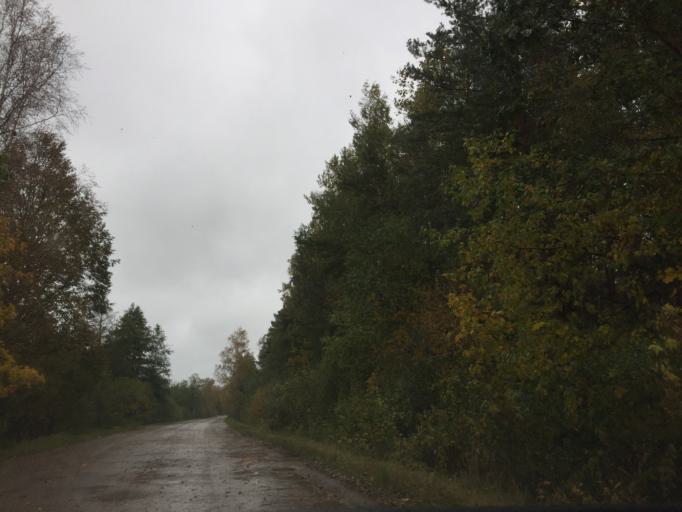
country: LV
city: Tireli
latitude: 56.8013
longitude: 23.5809
